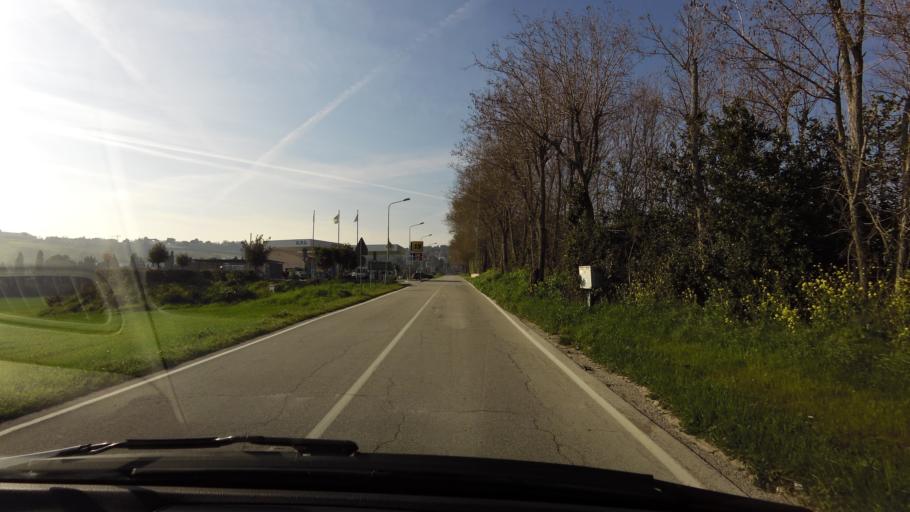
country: IT
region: The Marches
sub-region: Provincia di Ancona
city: Marcelli
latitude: 43.4979
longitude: 13.6201
